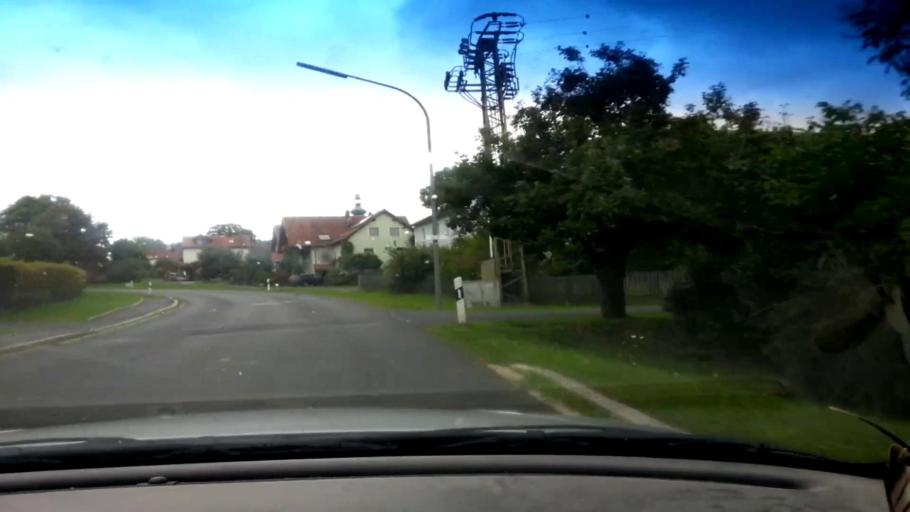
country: DE
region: Bavaria
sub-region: Upper Palatinate
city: Waldsassen
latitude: 50.0363
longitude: 12.2879
